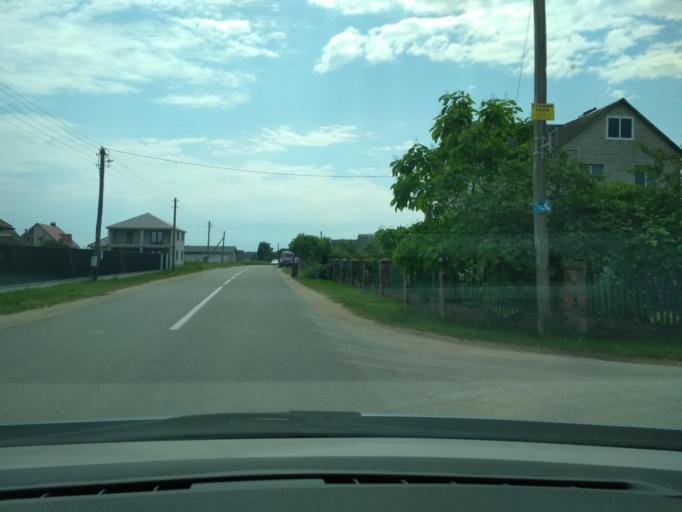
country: BY
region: Grodnenskaya
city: Astravyets
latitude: 54.6040
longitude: 25.9604
